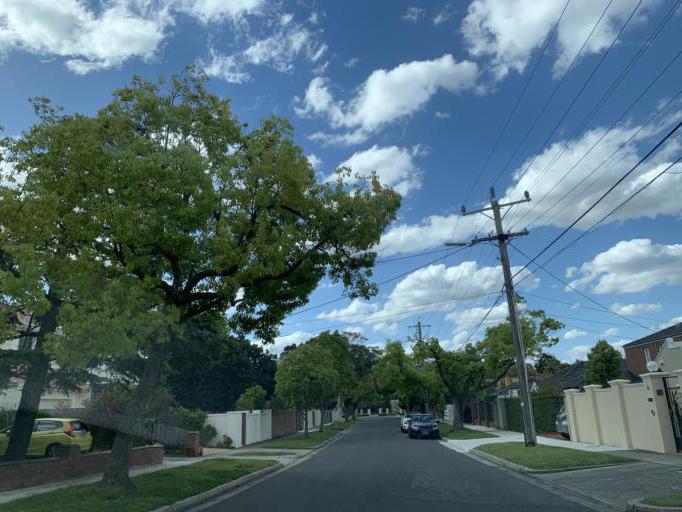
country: AU
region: Victoria
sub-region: Bayside
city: North Brighton
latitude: -37.9187
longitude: 145.0128
